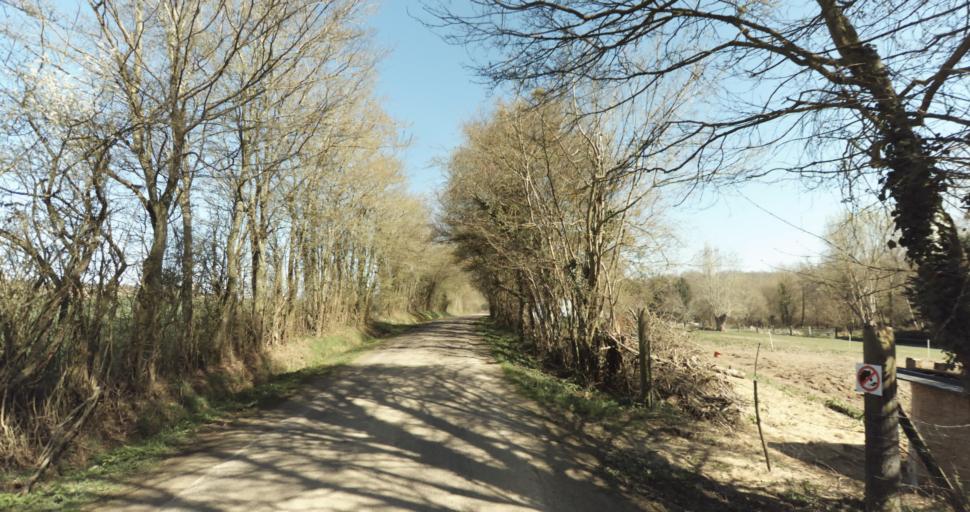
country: FR
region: Lower Normandy
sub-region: Departement du Calvados
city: Livarot
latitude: 49.0072
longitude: 0.0734
